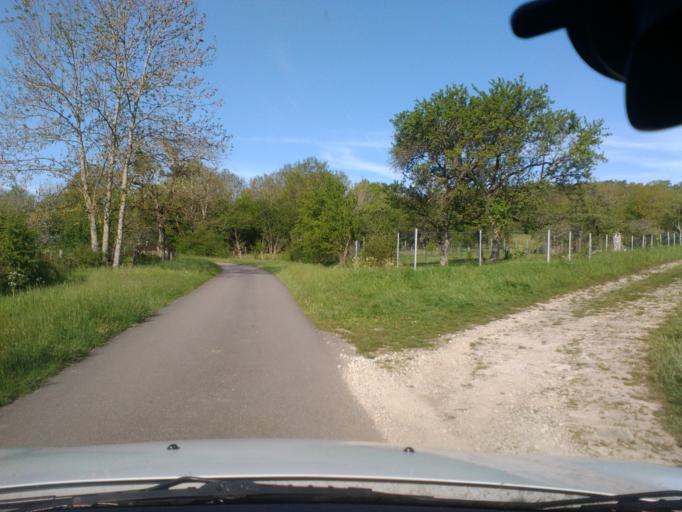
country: FR
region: Lorraine
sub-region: Departement des Vosges
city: Mirecourt
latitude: 48.2749
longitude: 6.1258
